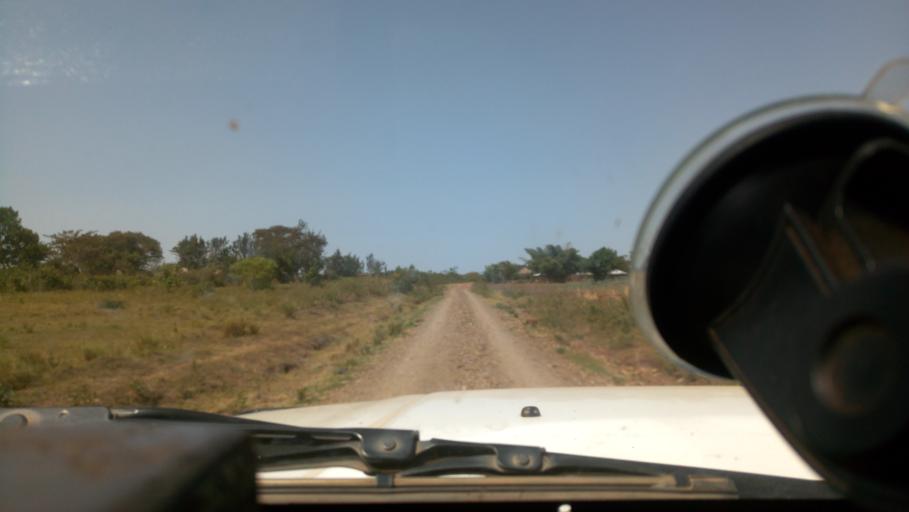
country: KE
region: Migori
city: Kihancha
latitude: -1.1665
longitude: 34.5854
